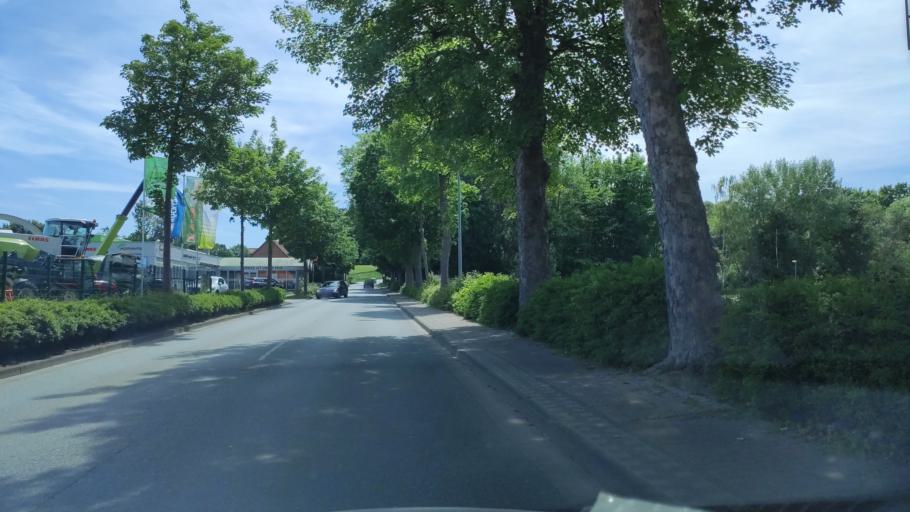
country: DE
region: North Rhine-Westphalia
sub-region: Regierungsbezirk Detmold
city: Steinheim
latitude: 51.8603
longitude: 9.0916
